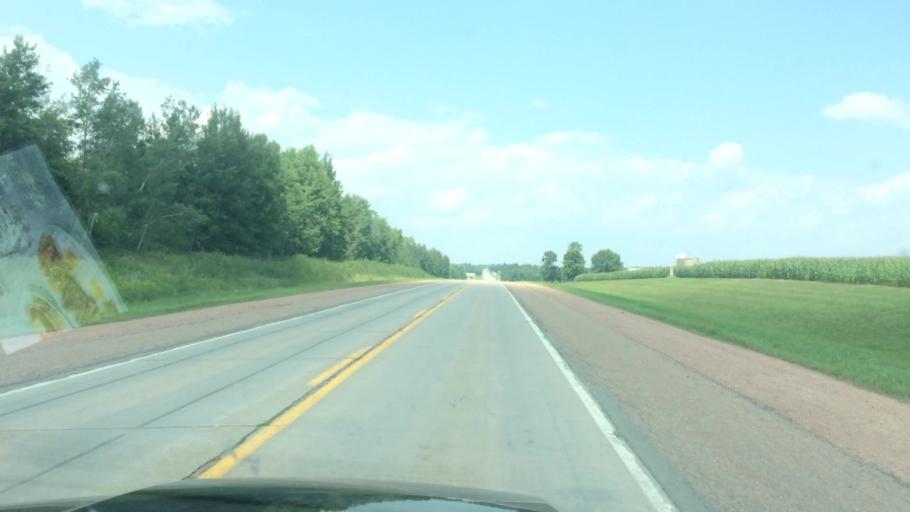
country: US
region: Wisconsin
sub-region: Clark County
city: Colby
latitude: 44.8810
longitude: -90.3156
